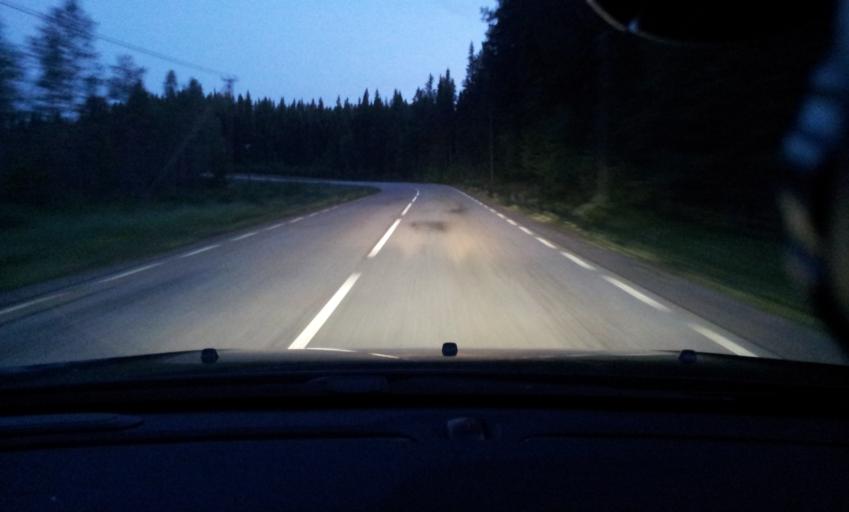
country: SE
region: Jaemtland
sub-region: OEstersunds Kommun
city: Brunflo
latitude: 62.6593
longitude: 14.9362
